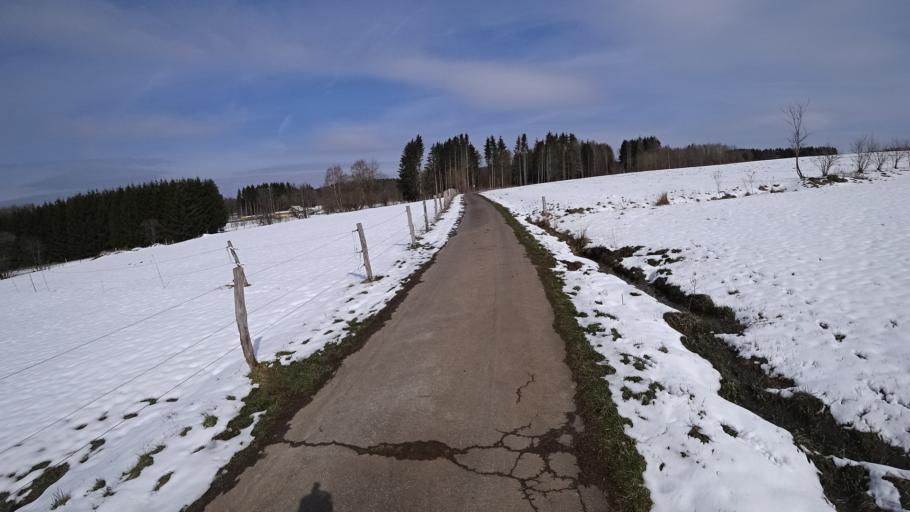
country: DE
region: Rheinland-Pfalz
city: Morlen
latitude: 50.7033
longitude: 7.8847
